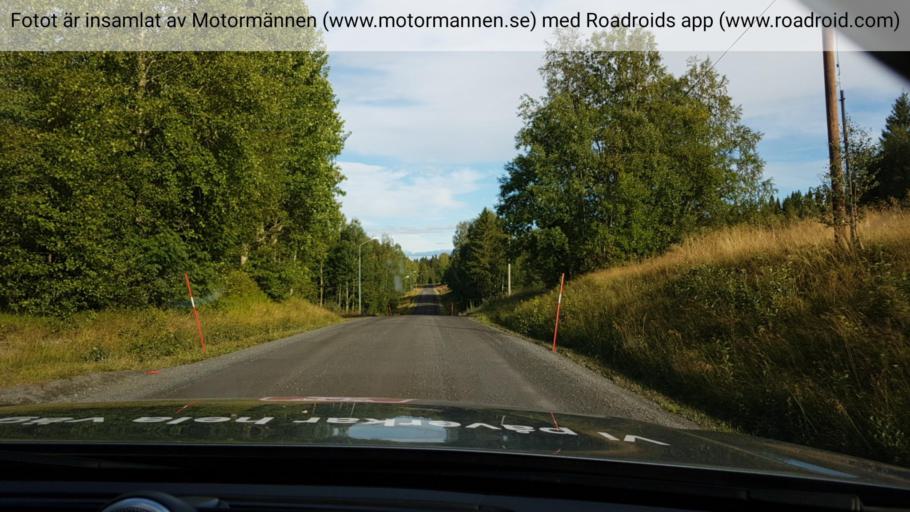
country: SE
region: Jaemtland
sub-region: Stroemsunds Kommun
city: Stroemsund
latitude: 64.1351
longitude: 15.7678
